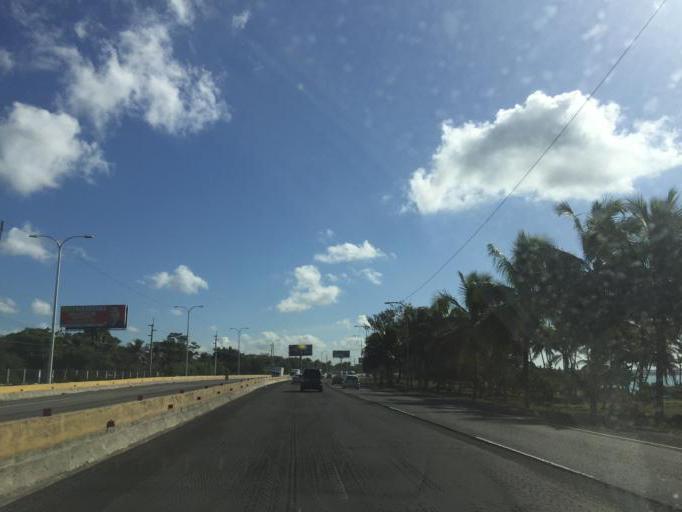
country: DO
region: Santo Domingo
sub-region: Santo Domingo
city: Boca Chica
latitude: 18.4553
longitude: -69.7006
